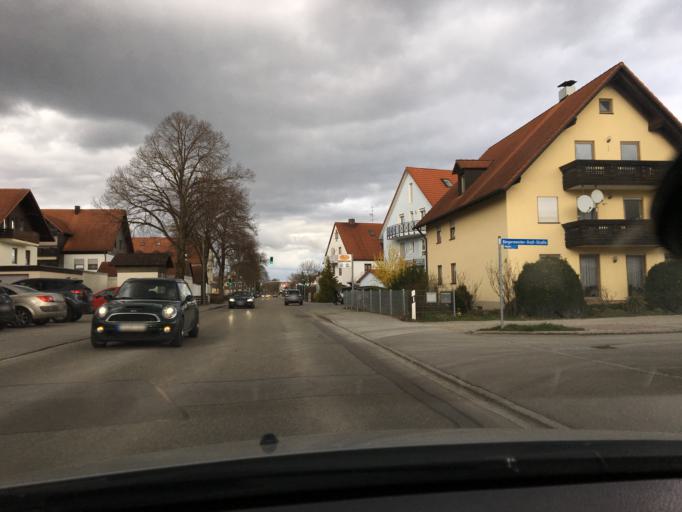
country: DE
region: Bavaria
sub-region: Upper Bavaria
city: Hallbergmoos
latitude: 48.3134
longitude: 11.7430
